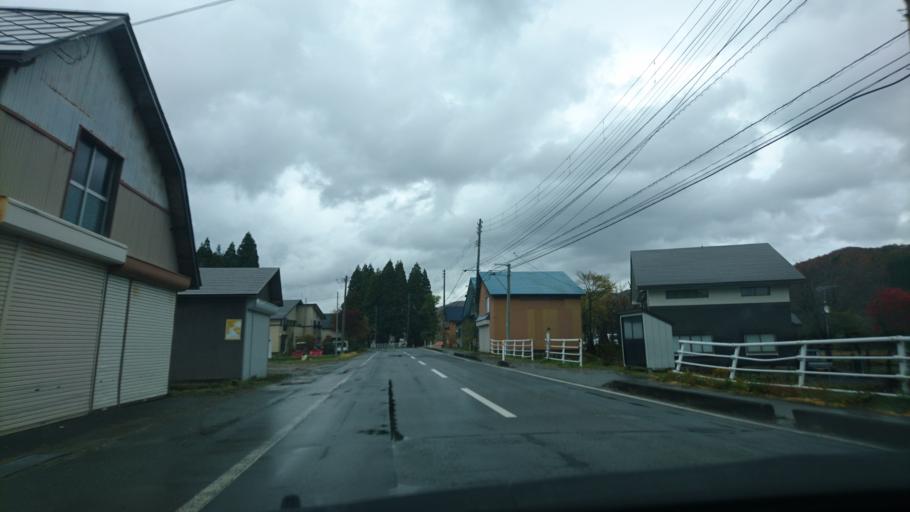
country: JP
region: Akita
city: Kakunodatemachi
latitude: 39.4902
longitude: 140.8101
